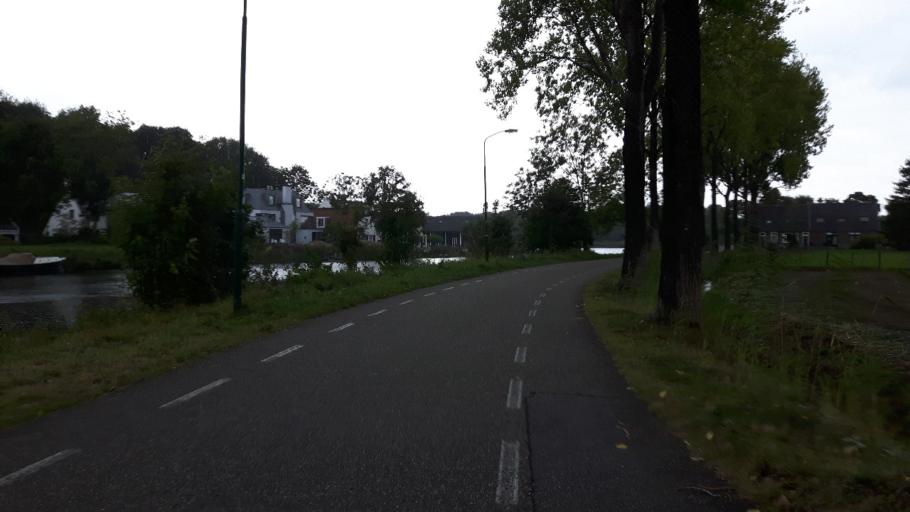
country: NL
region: Utrecht
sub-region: Stichtse Vecht
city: Maarssen
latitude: 52.1316
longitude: 5.0657
